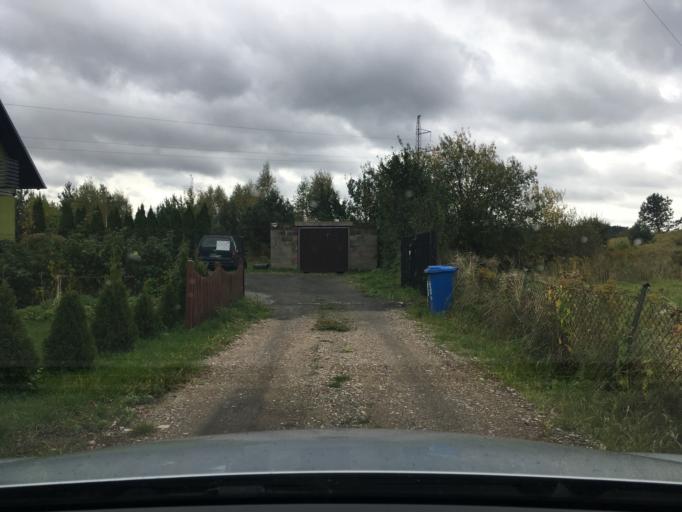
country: PL
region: Pomeranian Voivodeship
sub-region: Powiat koscierski
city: Koscierzyna
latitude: 54.1136
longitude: 18.0020
